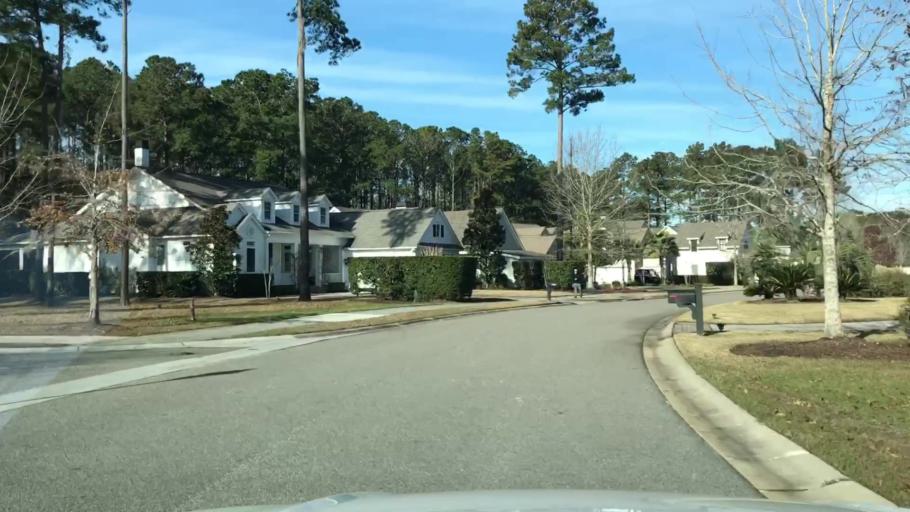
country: US
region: South Carolina
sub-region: Beaufort County
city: Bluffton
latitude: 32.2388
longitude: -80.9187
